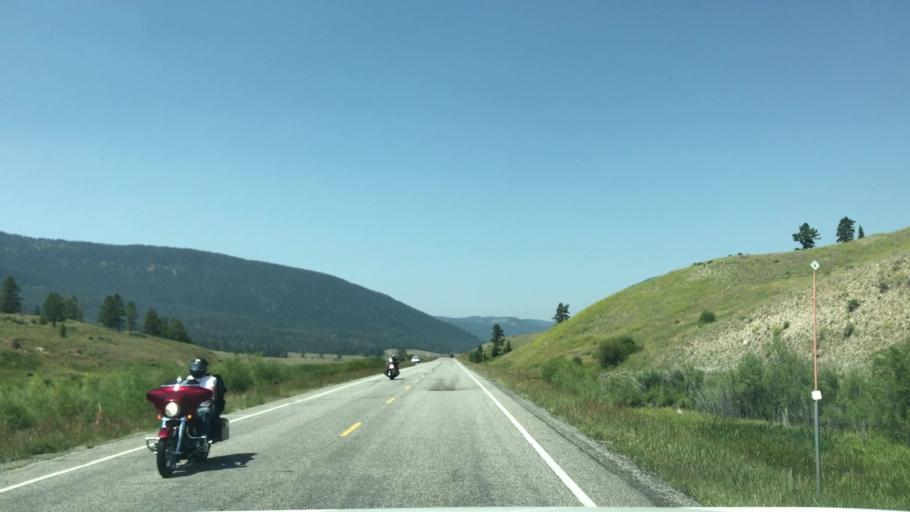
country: US
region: Montana
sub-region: Gallatin County
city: Big Sky
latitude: 45.0400
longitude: -111.1229
